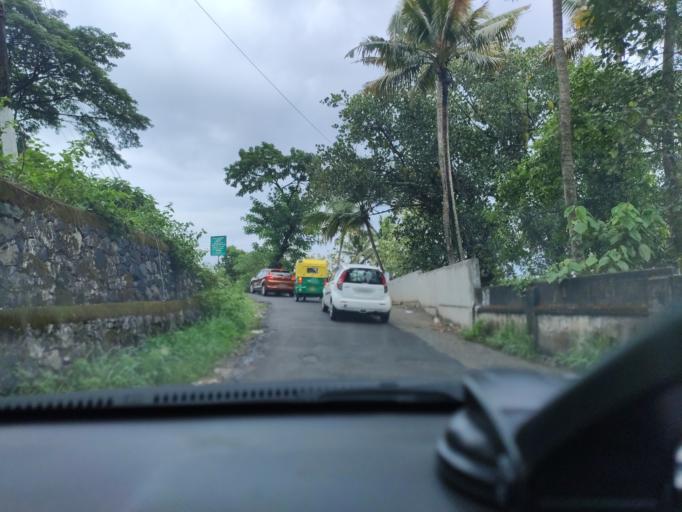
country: IN
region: Kerala
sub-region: Ernakulam
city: Elur
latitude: 10.0270
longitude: 76.3320
